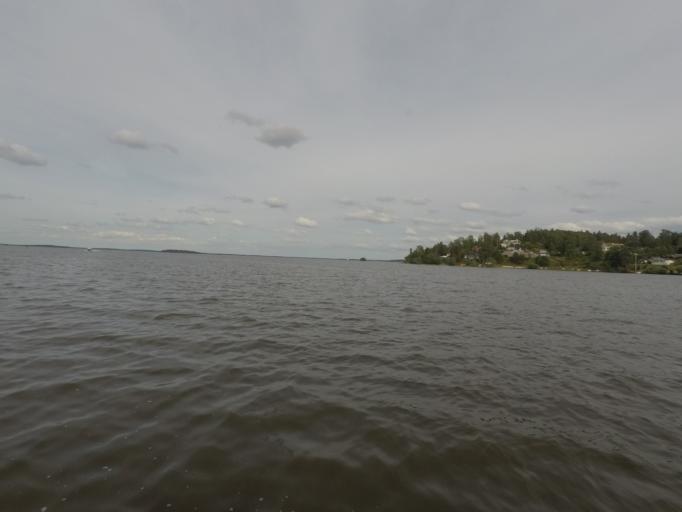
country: SE
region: Soedermanland
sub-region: Eskilstuna Kommun
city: Torshalla
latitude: 59.4609
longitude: 16.4524
